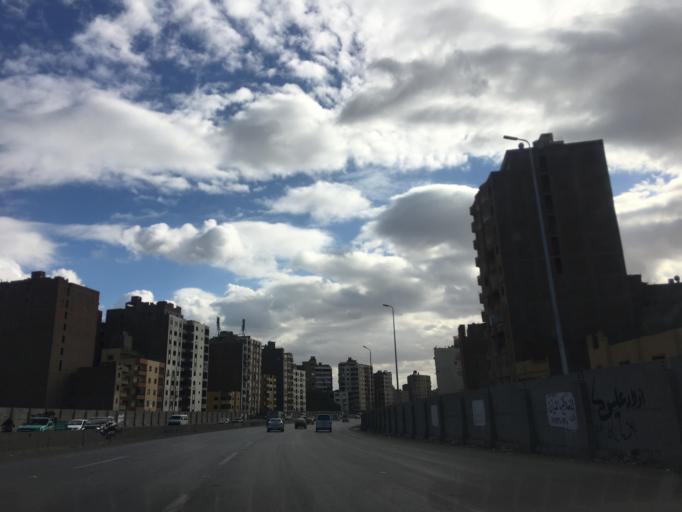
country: EG
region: Al Jizah
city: Al Jizah
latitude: 30.0218
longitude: 31.1659
